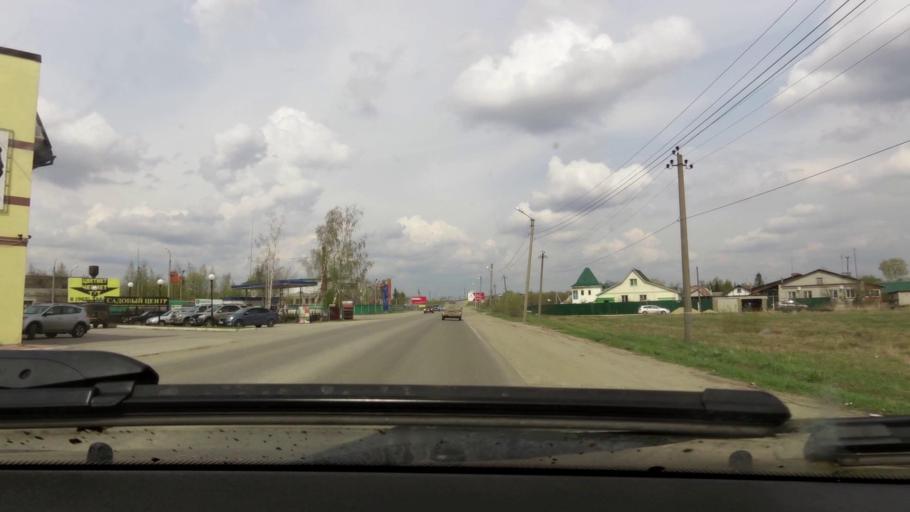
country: RU
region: Rjazan
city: Bagramovo
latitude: 54.7356
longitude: 39.4819
